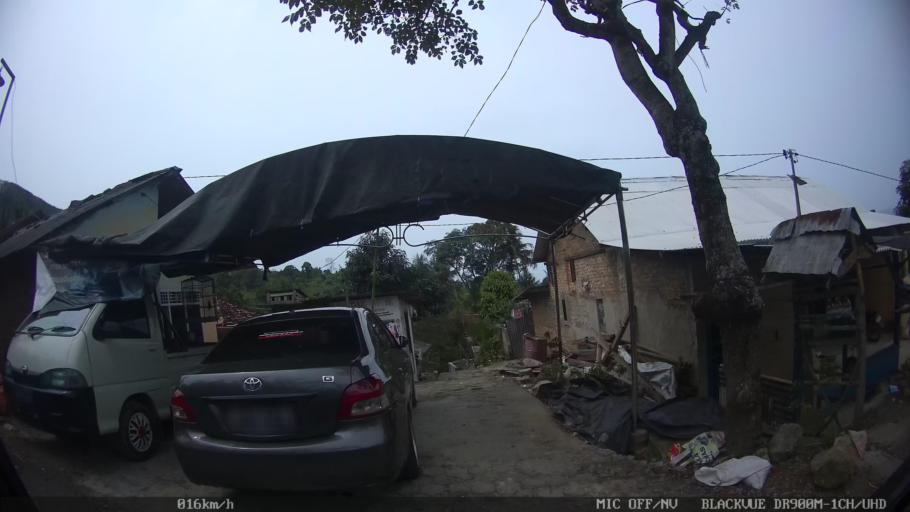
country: ID
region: Lampung
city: Bandarlampung
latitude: -5.4289
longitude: 105.2998
